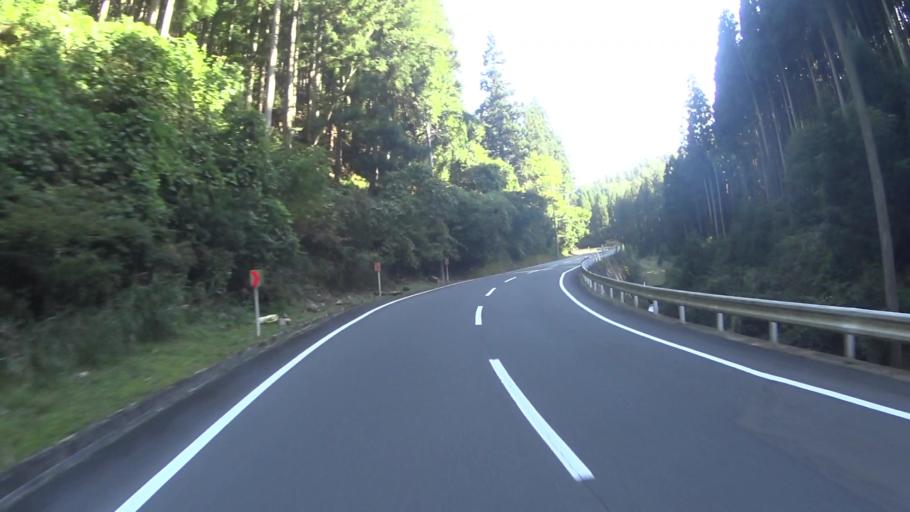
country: JP
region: Kyoto
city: Kameoka
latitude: 35.1238
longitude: 135.5596
